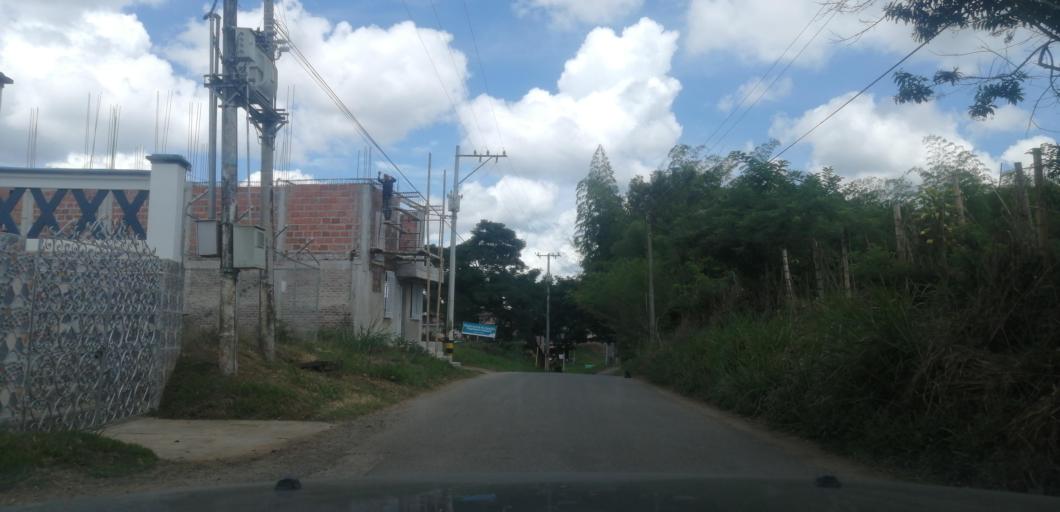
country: CO
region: Valle del Cauca
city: Restrepo
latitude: 3.8208
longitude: -76.5274
